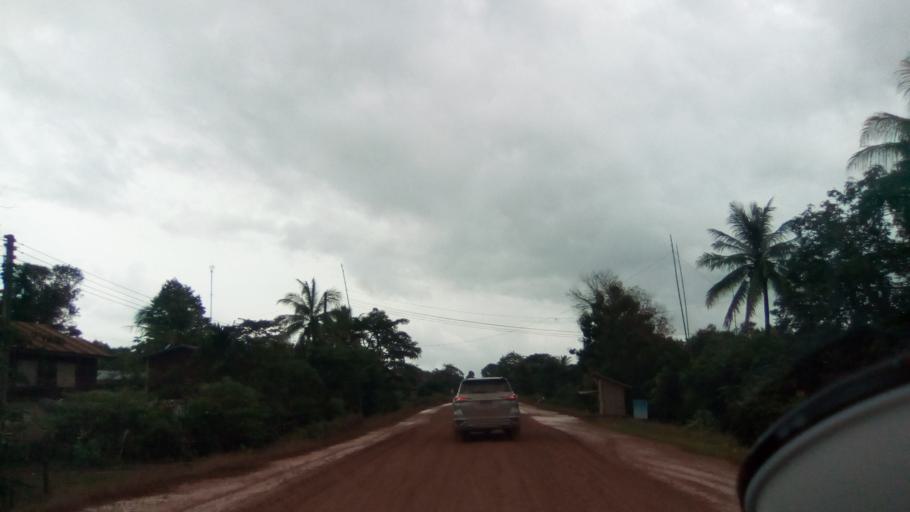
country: LA
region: Attapu
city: Attapu
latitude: 14.7480
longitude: 106.6990
